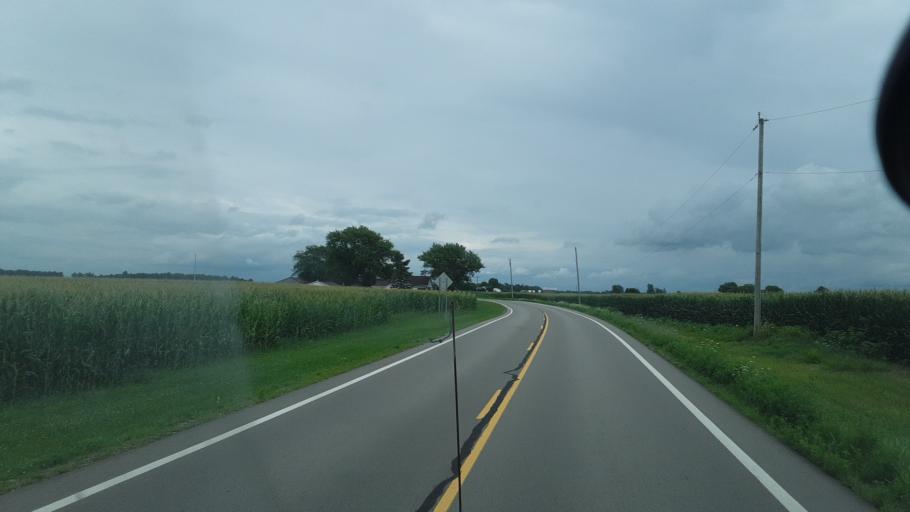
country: US
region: Ohio
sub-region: Logan County
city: Lakeview
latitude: 40.5560
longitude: -83.9501
